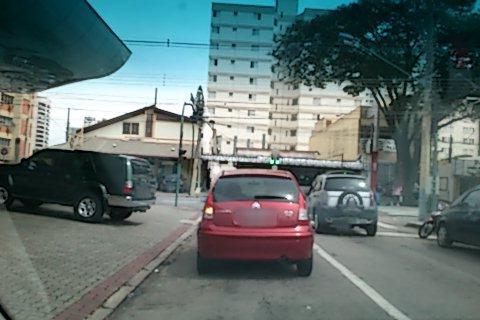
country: BR
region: Sao Paulo
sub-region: Sao Jose Dos Campos
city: Sao Jose dos Campos
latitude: -23.2015
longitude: -45.8925
